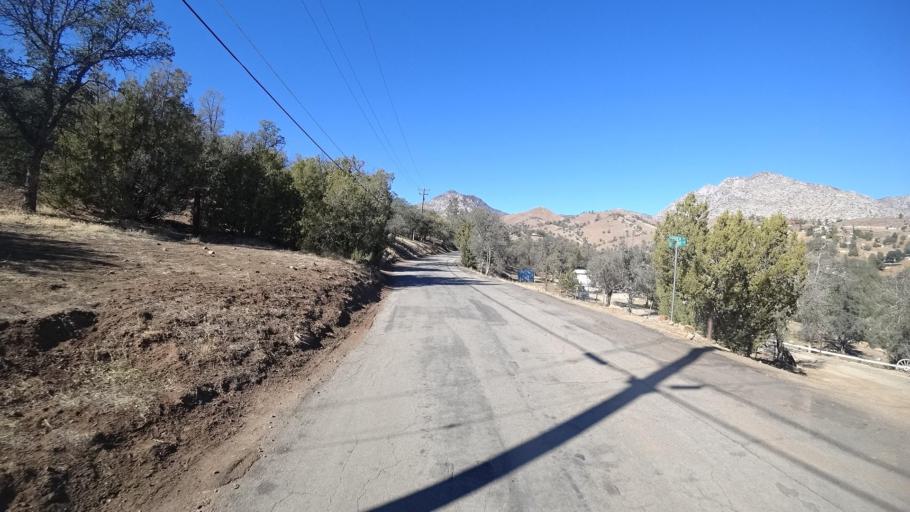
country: US
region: California
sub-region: Kern County
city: Wofford Heights
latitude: 35.7073
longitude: -118.4693
